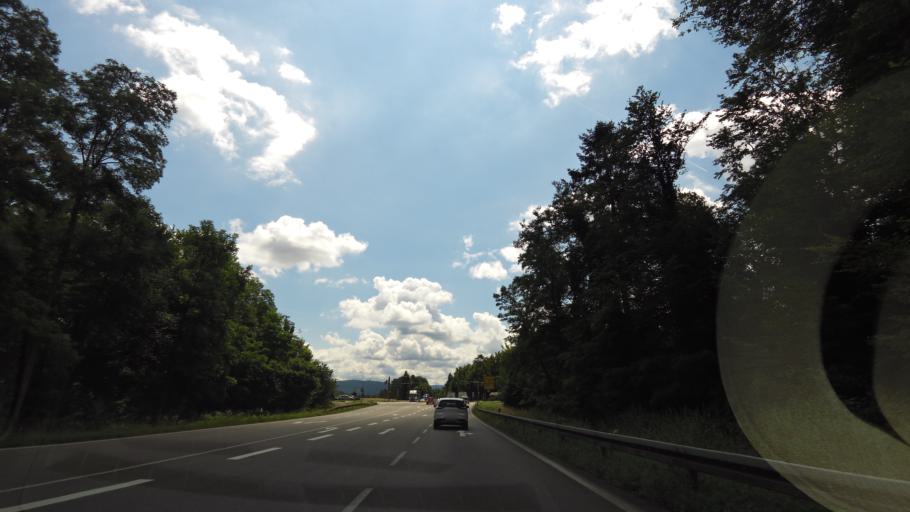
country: DE
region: Baden-Wuerttemberg
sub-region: Karlsruhe Region
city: Iffezheim
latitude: 48.8097
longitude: 8.1369
